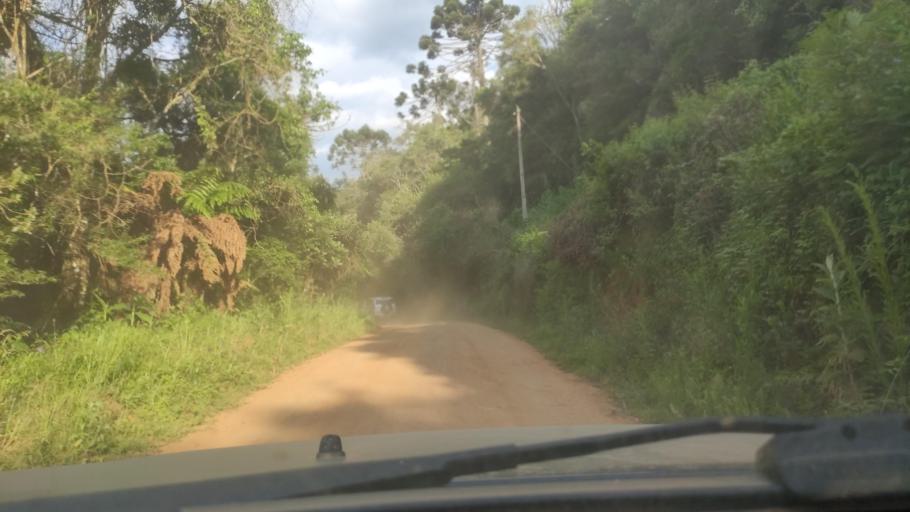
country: BR
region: Minas Gerais
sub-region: Cambui
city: Cambui
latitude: -22.7574
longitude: -45.9510
